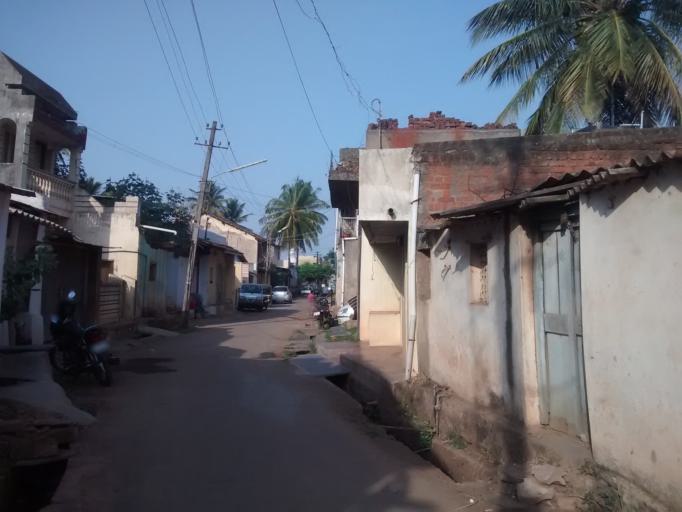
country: IN
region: Karnataka
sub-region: Dharwad
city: Hubli
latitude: 15.4541
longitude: 75.0188
